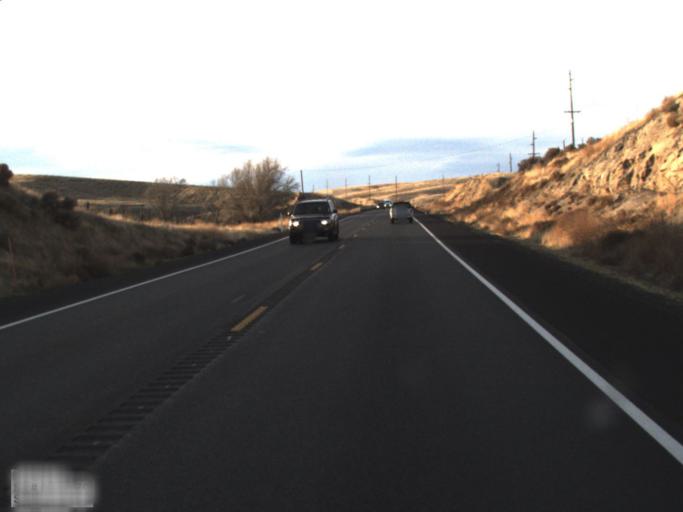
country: US
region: Washington
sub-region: Walla Walla County
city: Garrett
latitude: 46.0497
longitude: -118.7037
